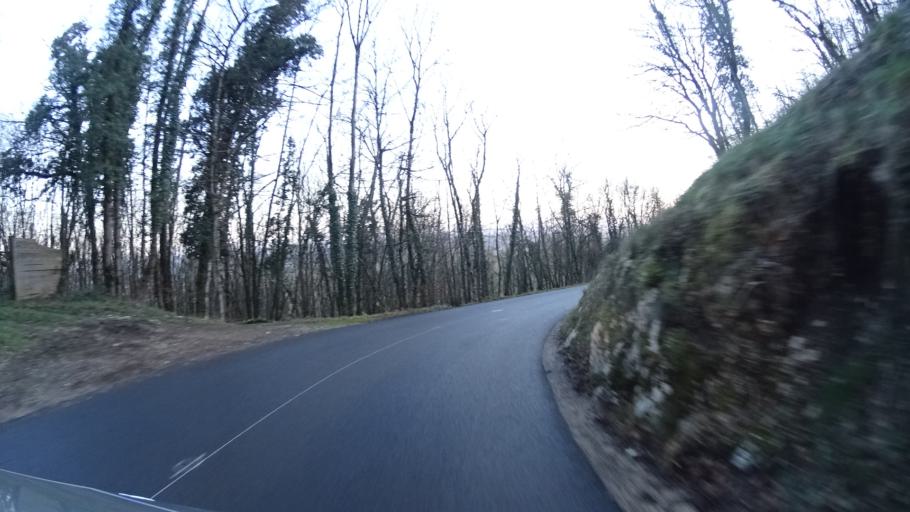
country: FR
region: Franche-Comte
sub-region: Departement du Doubs
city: Morre
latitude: 47.2116
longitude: 6.0548
